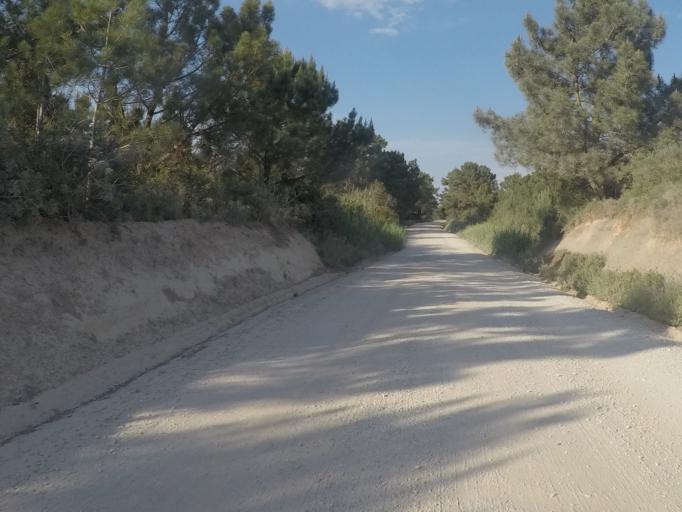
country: PT
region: Setubal
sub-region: Sesimbra
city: Sesimbra
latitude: 38.4540
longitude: -9.1919
